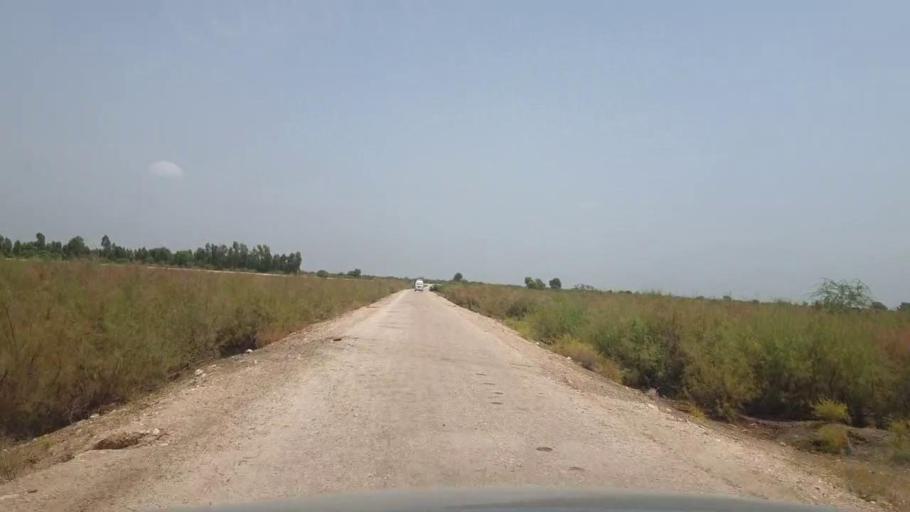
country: PK
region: Sindh
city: Garhi Yasin
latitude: 27.9558
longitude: 68.4393
